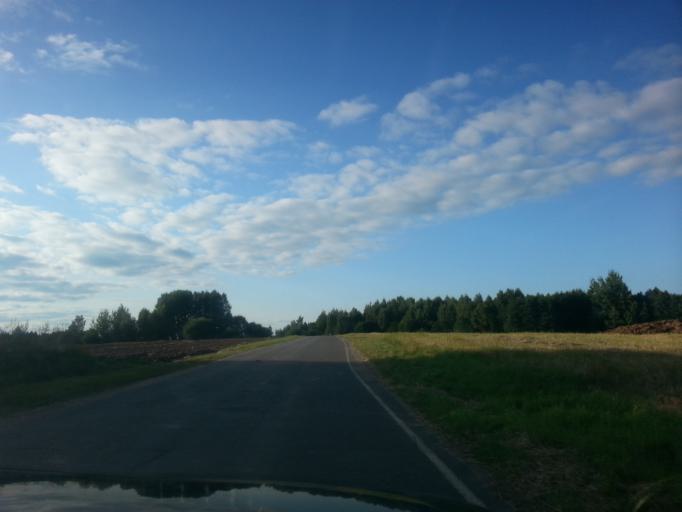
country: BY
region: Minsk
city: Narach
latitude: 54.9665
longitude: 26.6389
